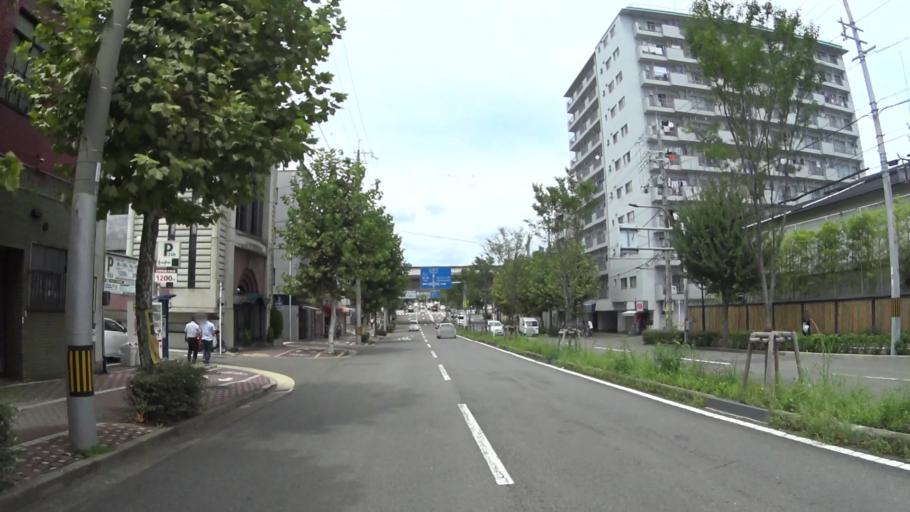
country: JP
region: Kyoto
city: Kyoto
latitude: 35.0168
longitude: 135.7317
